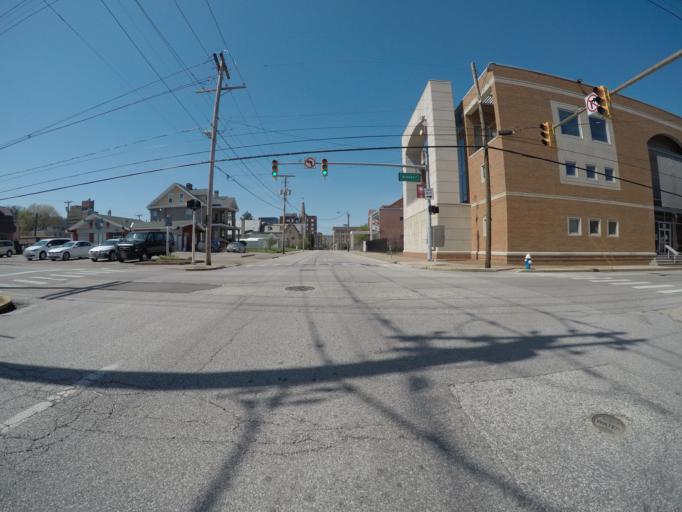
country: US
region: West Virginia
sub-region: Kanawha County
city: Charleston
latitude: 38.3463
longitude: -81.6303
